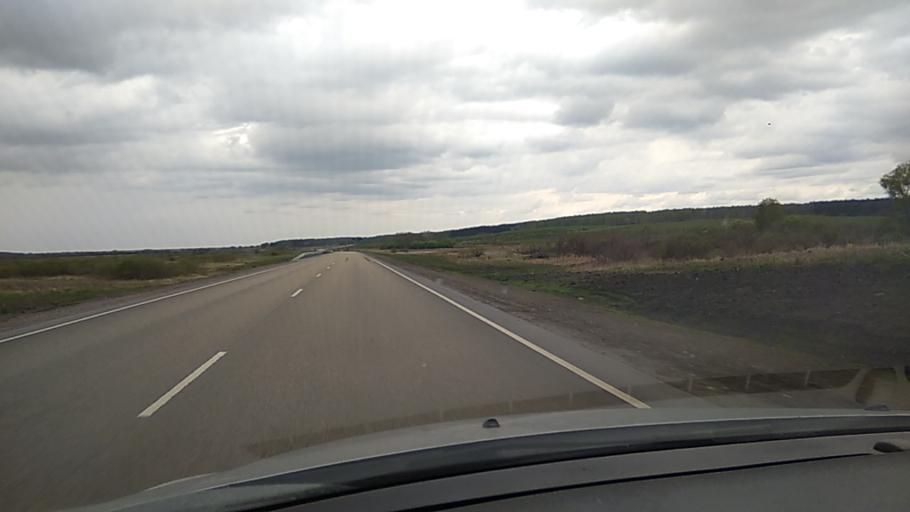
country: RU
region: Kurgan
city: Kataysk
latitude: 56.2976
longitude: 62.4256
